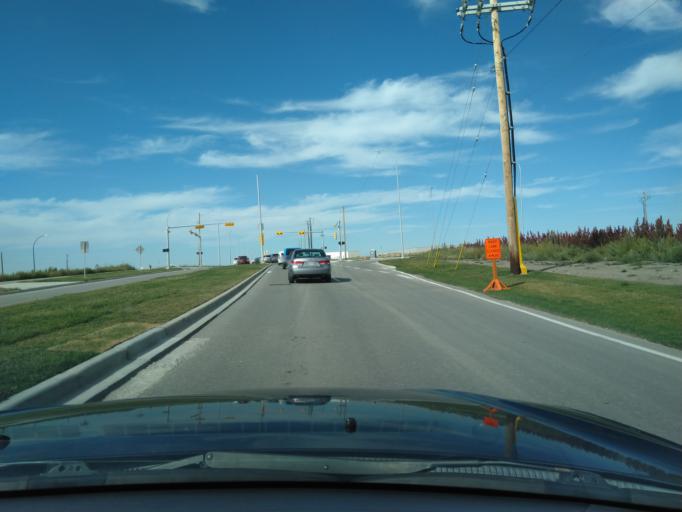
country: CA
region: Alberta
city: Calgary
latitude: 51.1243
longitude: -113.9817
